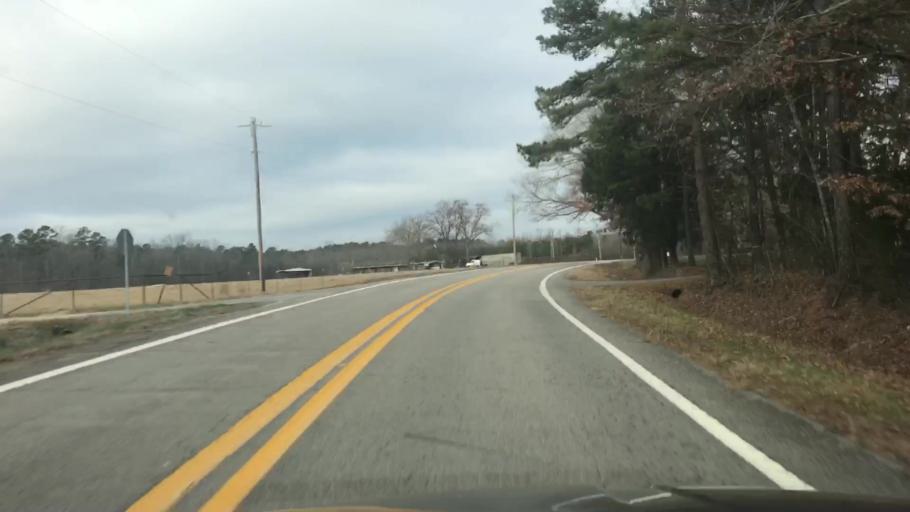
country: US
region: Arkansas
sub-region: Montgomery County
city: Mount Ida
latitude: 34.6611
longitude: -93.7687
